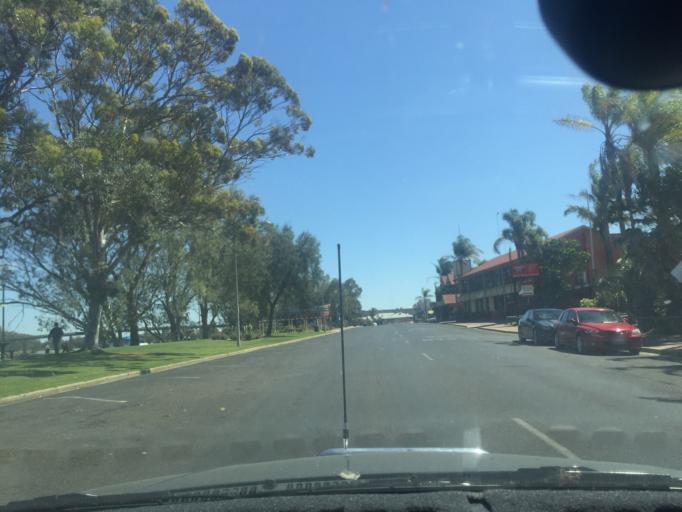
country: AU
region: South Australia
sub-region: Berri and Barmera
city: Berri
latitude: -34.2875
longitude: 140.6052
